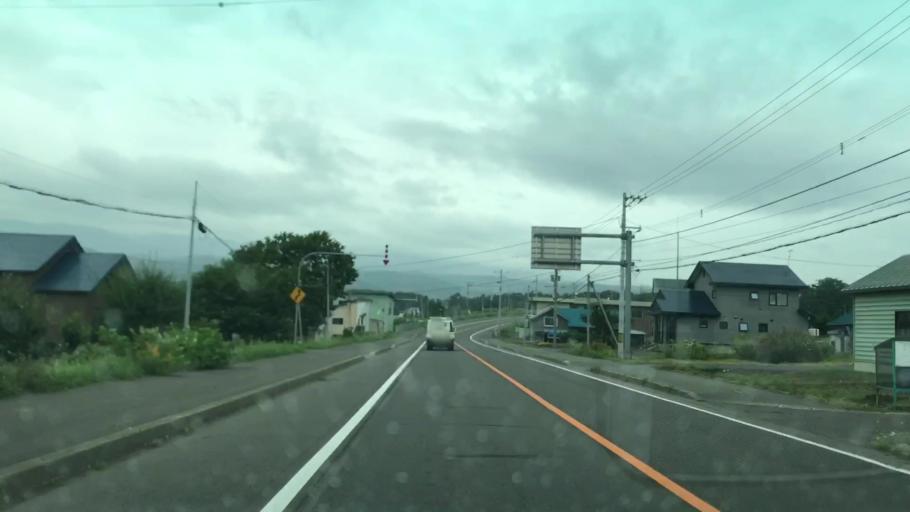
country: JP
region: Hokkaido
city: Niseko Town
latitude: 42.8092
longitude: 140.5326
